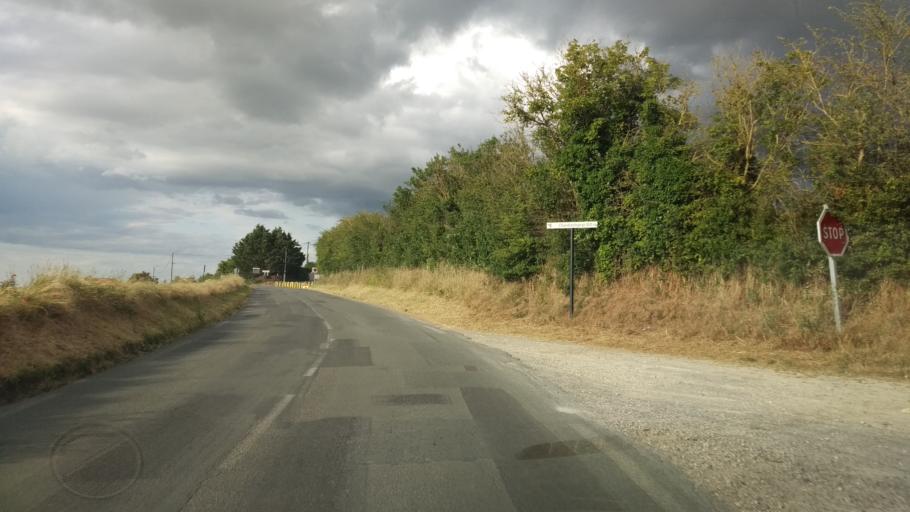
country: FR
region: Poitou-Charentes
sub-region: Departement de la Vienne
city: Migne-Auxances
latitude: 46.6261
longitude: 0.3298
